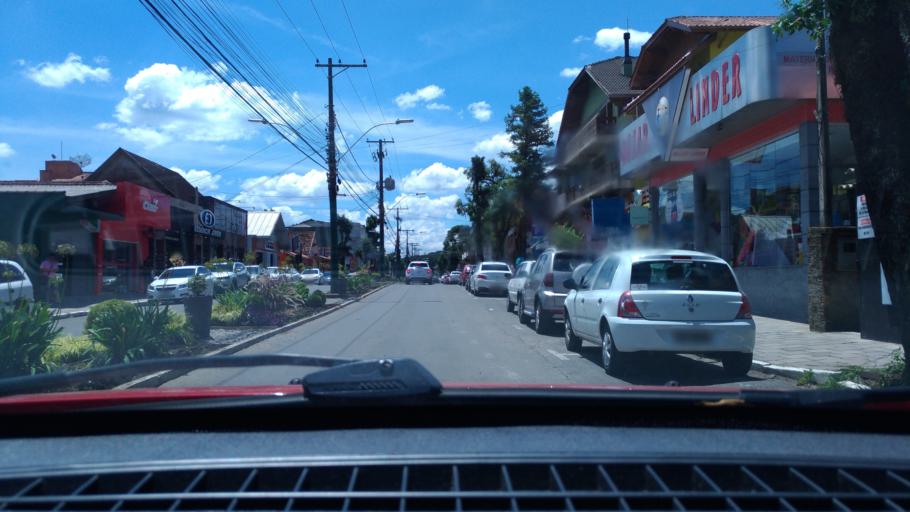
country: BR
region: Rio Grande do Sul
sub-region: Canela
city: Canela
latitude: -29.3629
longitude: -50.8128
